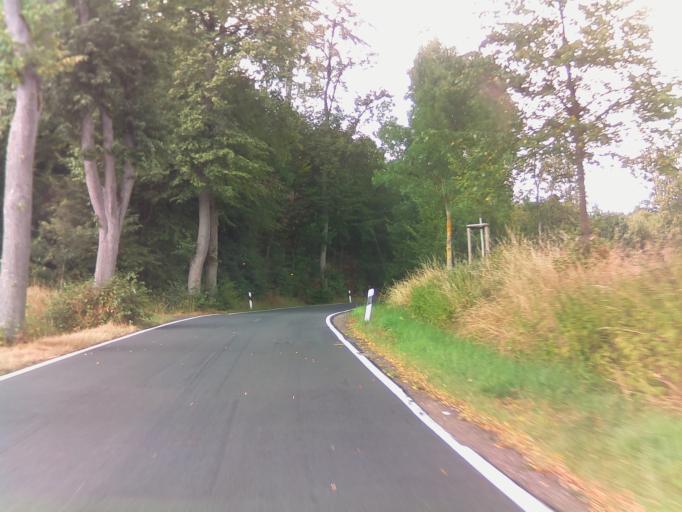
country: DE
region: Hesse
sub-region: Regierungsbezirk Giessen
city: Lauterbach
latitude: 50.5714
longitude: 9.4332
